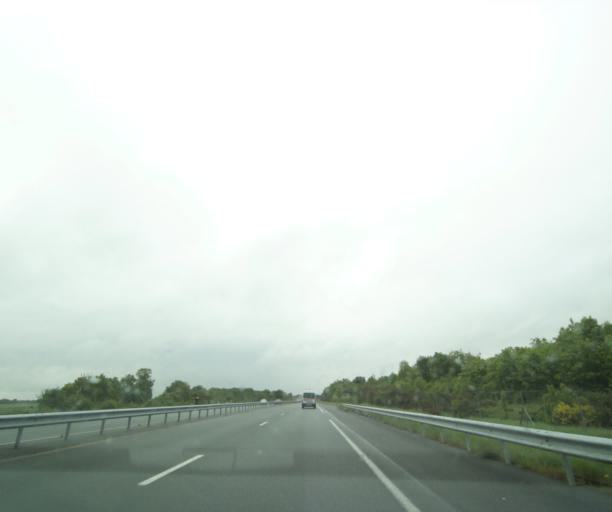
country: FR
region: Poitou-Charentes
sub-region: Departement de la Charente-Maritime
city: Nieul-les-Saintes
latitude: 45.7028
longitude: -0.7565
